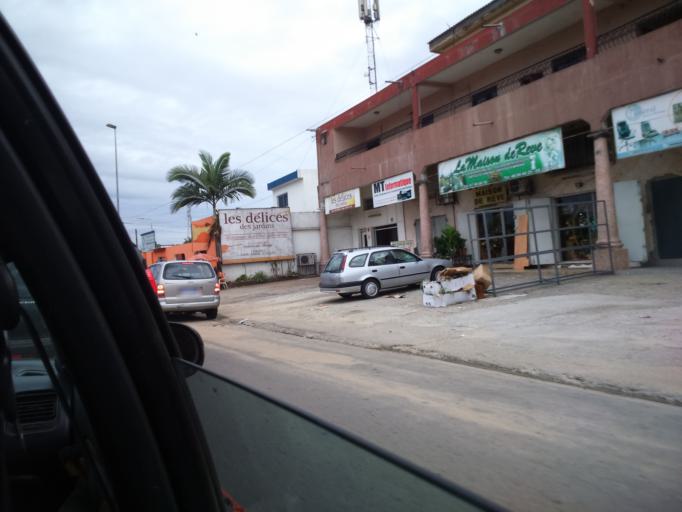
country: CI
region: Lagunes
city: Abidjan
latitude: 5.3557
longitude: -3.9918
